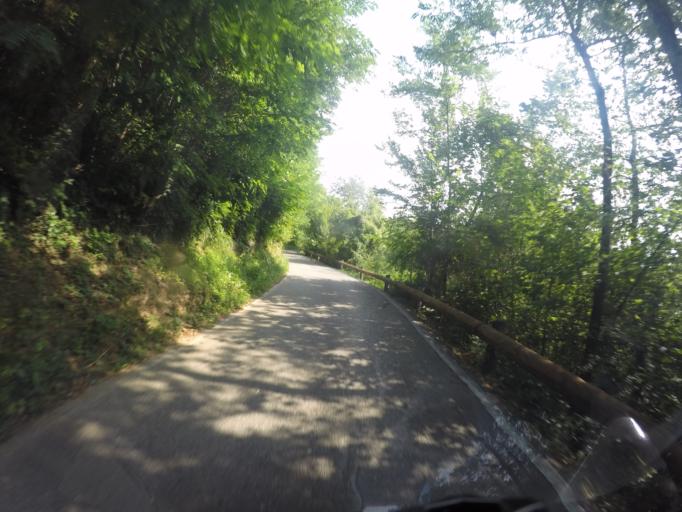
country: IT
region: Lombardy
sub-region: Provincia di Lecco
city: Olgiate Molgora
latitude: 45.7529
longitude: 9.3970
